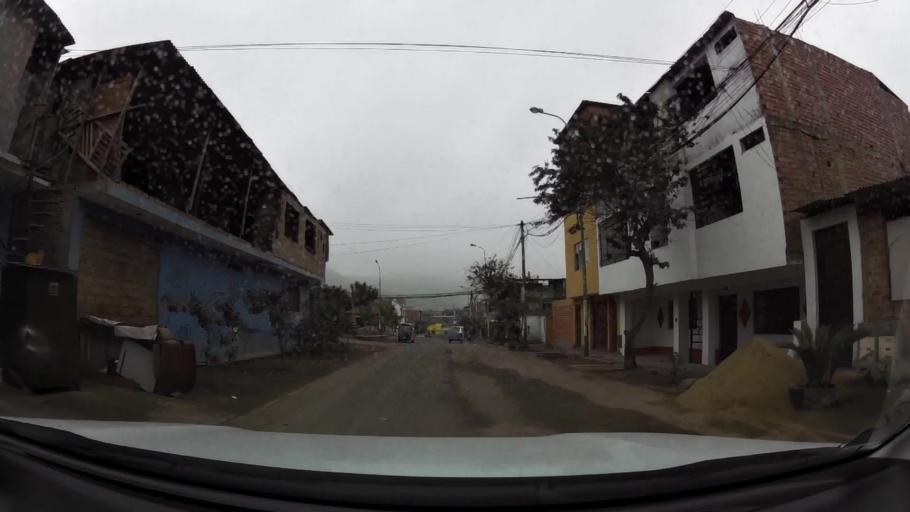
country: PE
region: Lima
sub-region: Lima
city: Surco
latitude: -12.1694
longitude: -76.9524
